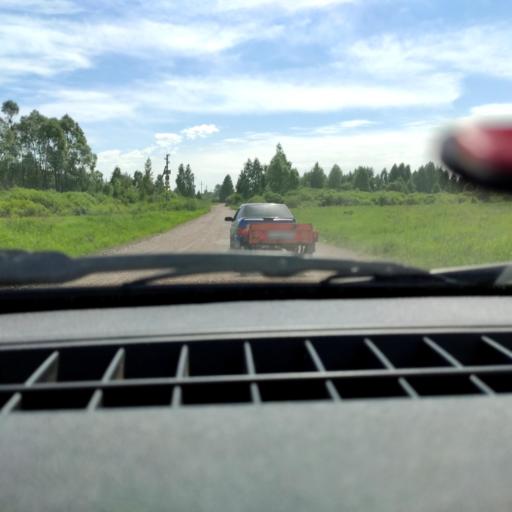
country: RU
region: Bashkortostan
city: Kabakovo
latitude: 54.7330
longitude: 56.2002
